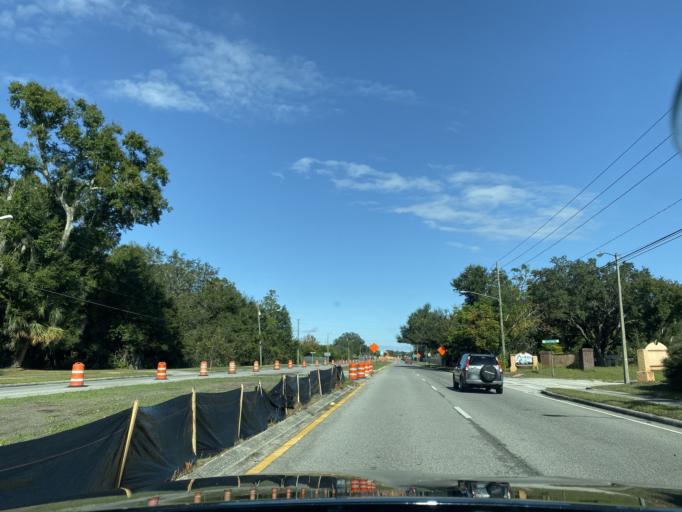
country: US
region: Florida
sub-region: Orange County
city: Alafaya
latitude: 28.5854
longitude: -81.2450
